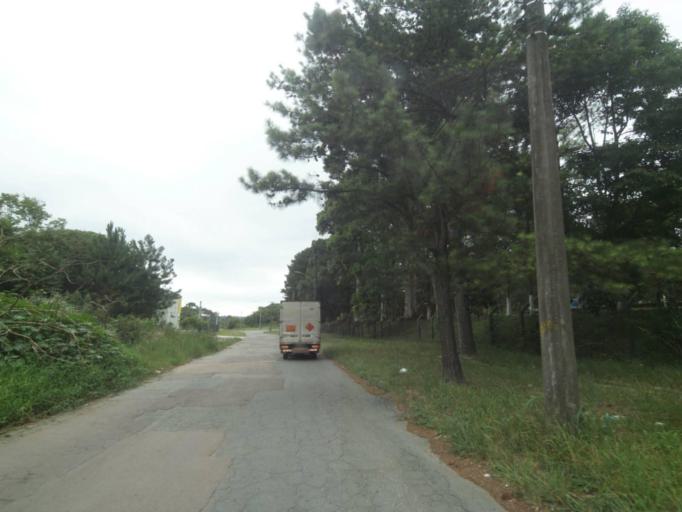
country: BR
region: Parana
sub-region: Araucaria
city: Araucaria
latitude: -25.5406
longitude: -49.3191
